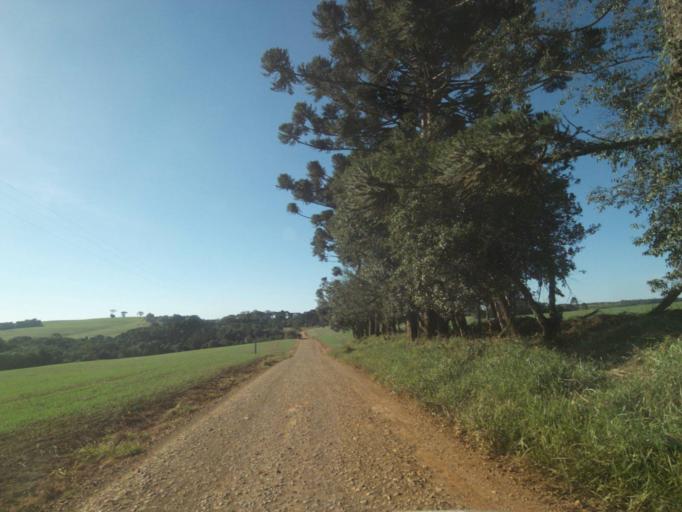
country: BR
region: Parana
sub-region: Tibagi
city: Tibagi
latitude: -24.5395
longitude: -50.4979
